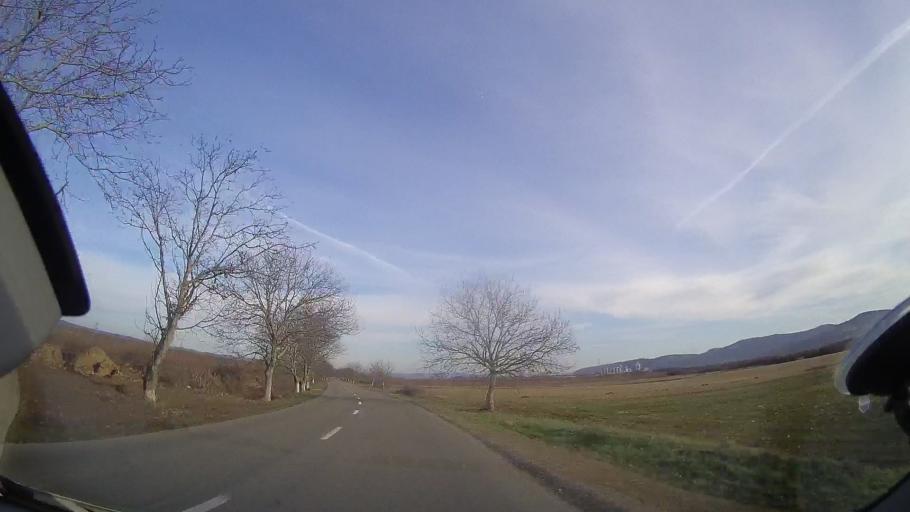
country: RO
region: Bihor
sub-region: Comuna Tetchea
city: Hotar
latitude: 47.0518
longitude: 22.2966
